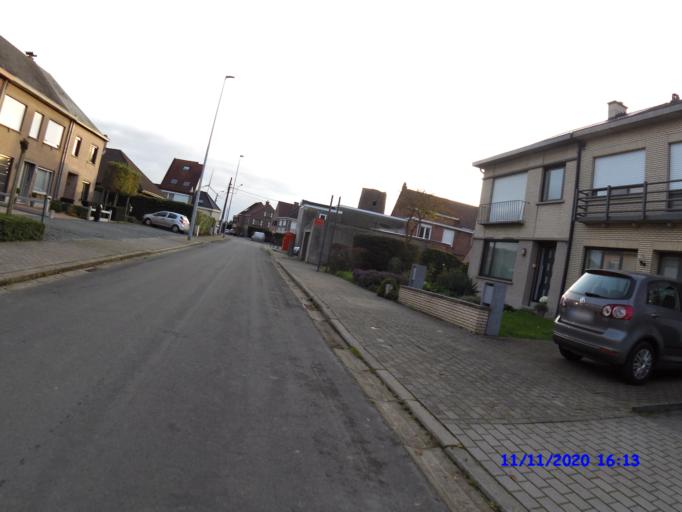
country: BE
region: Flanders
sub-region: Provincie Oost-Vlaanderen
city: Lebbeke
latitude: 51.0345
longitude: 4.1541
